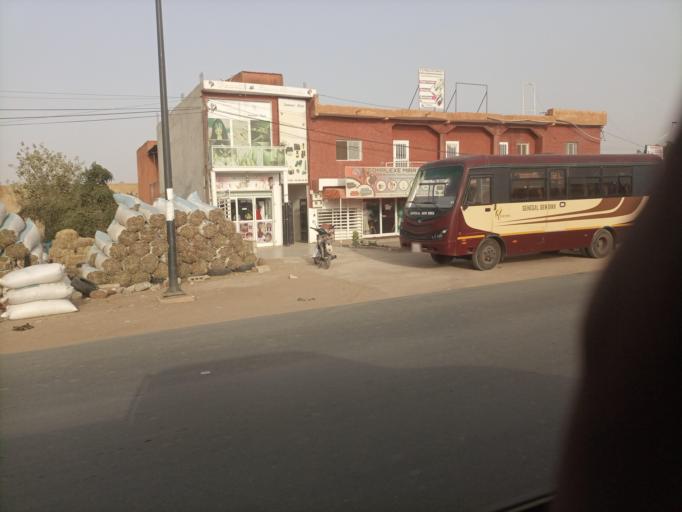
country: SN
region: Thies
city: Warang
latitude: 14.4394
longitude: -16.9783
